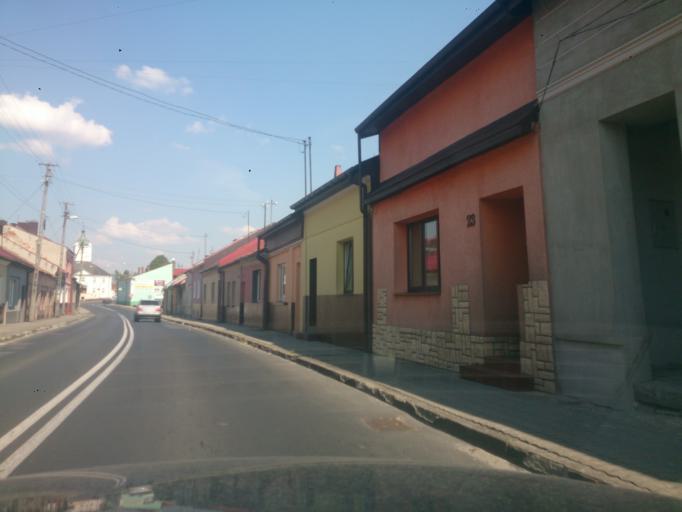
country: PL
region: Subcarpathian Voivodeship
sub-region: Powiat rzeszowski
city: Glogow Malopolski
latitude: 50.1492
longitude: 21.9626
